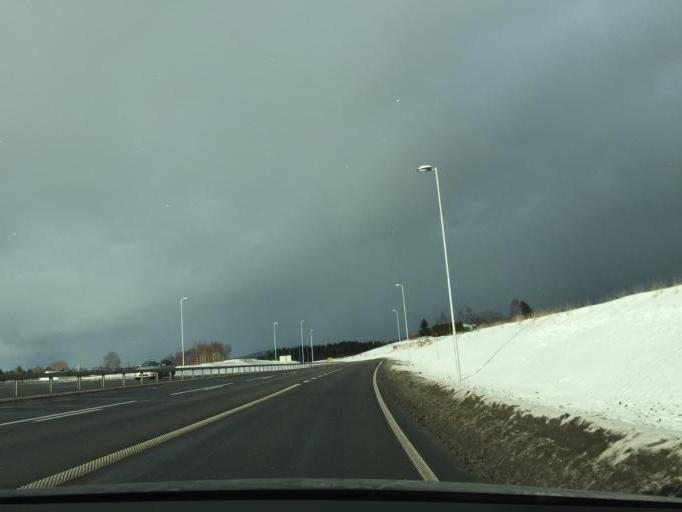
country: NO
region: Hedmark
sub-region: Kongsvinger
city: Spetalen
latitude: 60.2097
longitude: 11.8873
